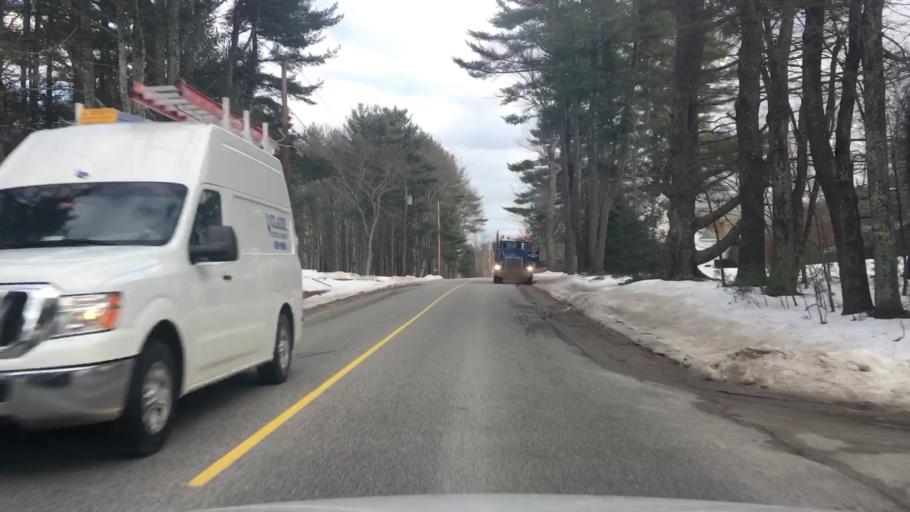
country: US
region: Maine
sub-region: York County
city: Kennebunk
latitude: 43.4053
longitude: -70.5181
